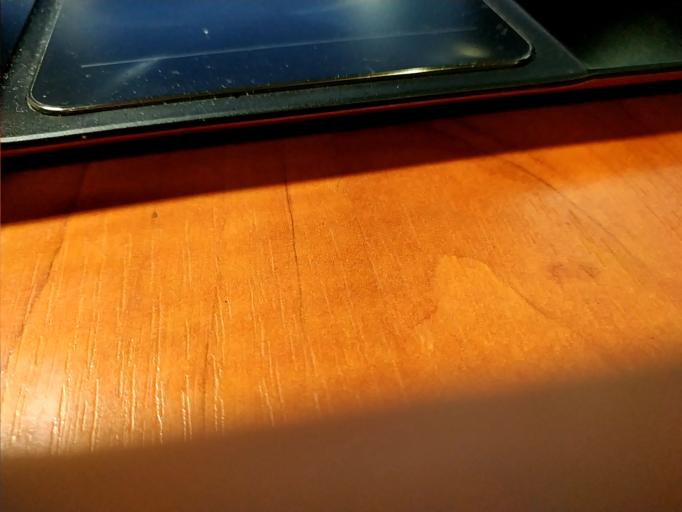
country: RU
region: Rjazan
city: Pronsk
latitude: 54.0556
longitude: 39.4163
